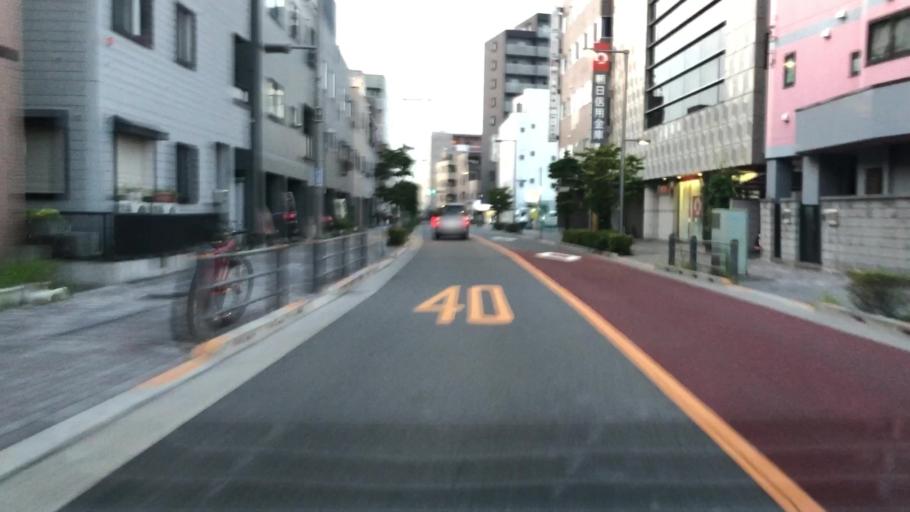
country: JP
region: Saitama
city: Soka
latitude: 35.7396
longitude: 139.7735
